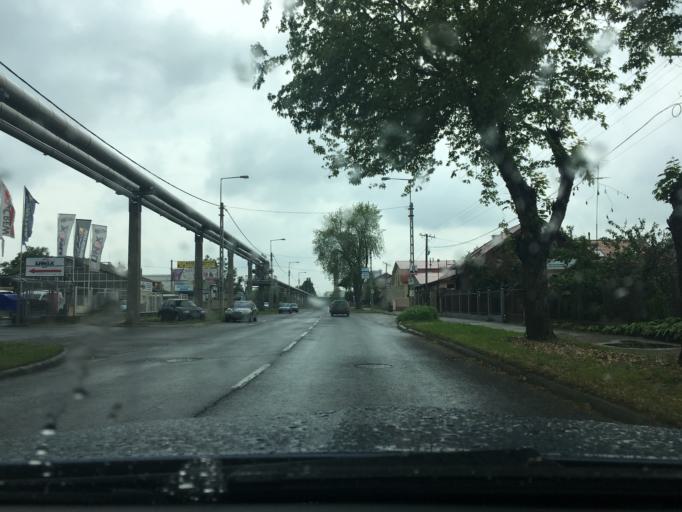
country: HU
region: Hajdu-Bihar
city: Debrecen
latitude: 47.5129
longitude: 21.6379
